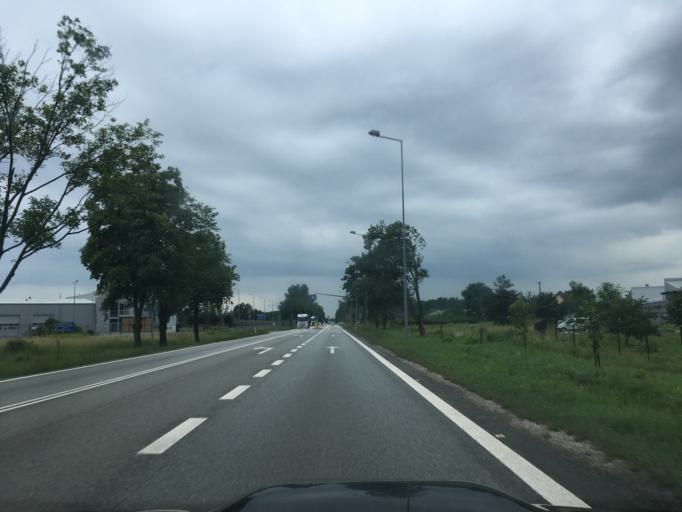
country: PL
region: Masovian Voivodeship
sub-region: Powiat otwocki
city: Karczew
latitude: 52.0185
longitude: 21.2930
